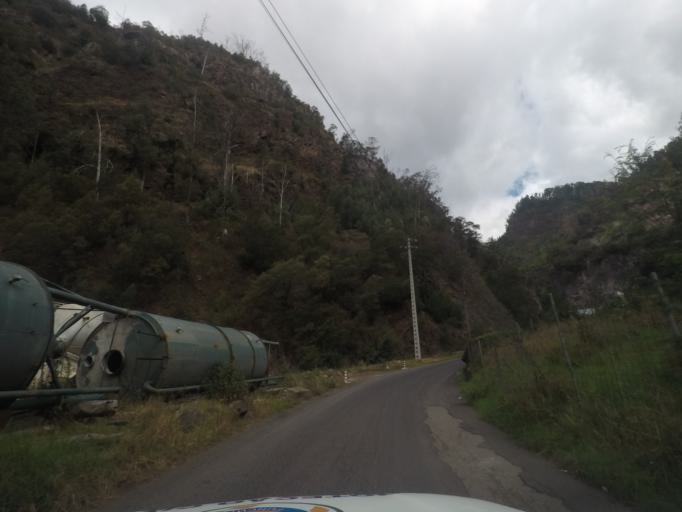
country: PT
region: Madeira
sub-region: Funchal
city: Nossa Senhora do Monte
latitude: 32.6818
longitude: -16.9155
